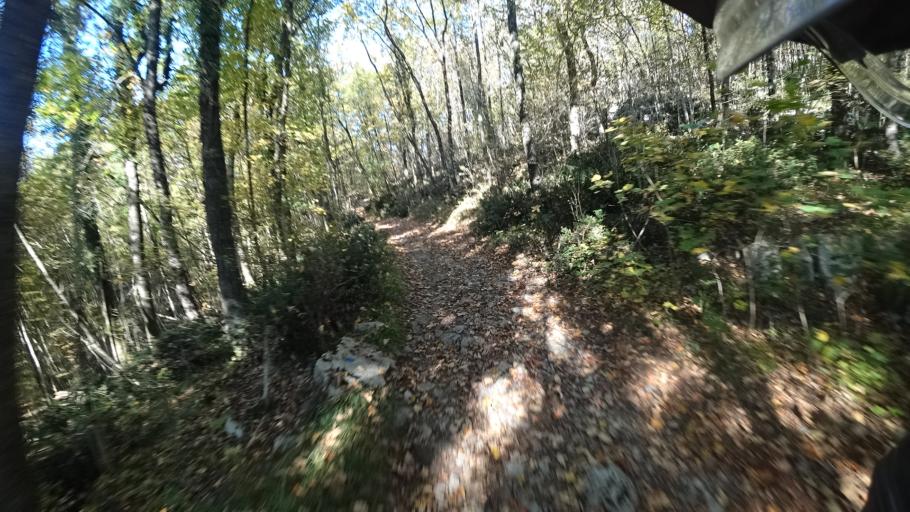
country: HR
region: Primorsko-Goranska
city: Kastav
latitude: 45.4002
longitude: 14.3257
